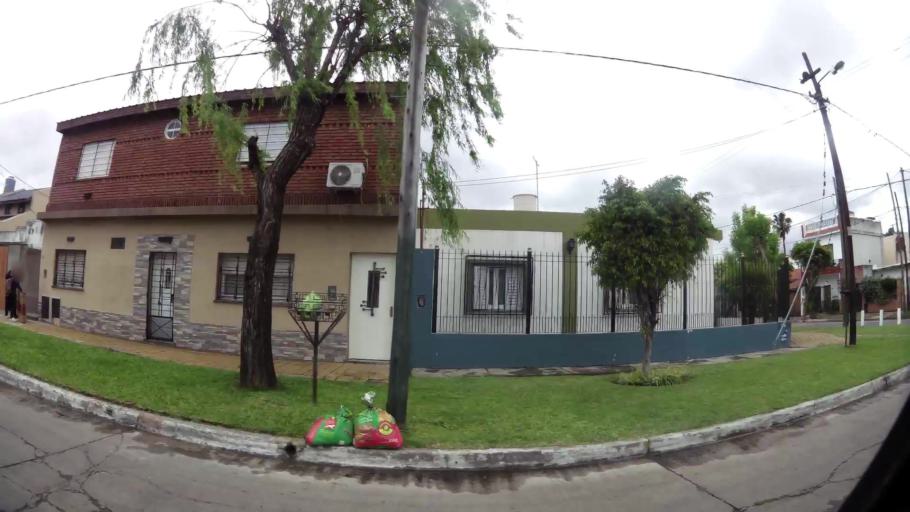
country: AR
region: Buenos Aires
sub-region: Partido de Lomas de Zamora
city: Lomas de Zamora
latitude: -34.7476
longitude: -58.3812
